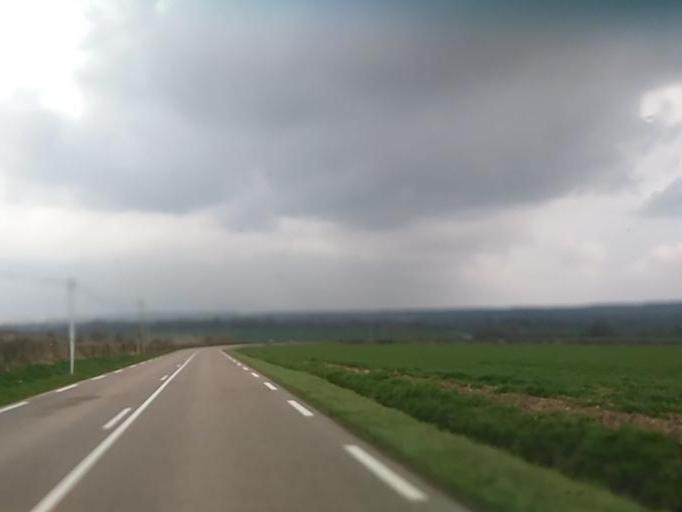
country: FR
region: Lower Normandy
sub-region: Departement de l'Orne
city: Pont-Ecrepin
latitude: 48.8244
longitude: -0.2411
